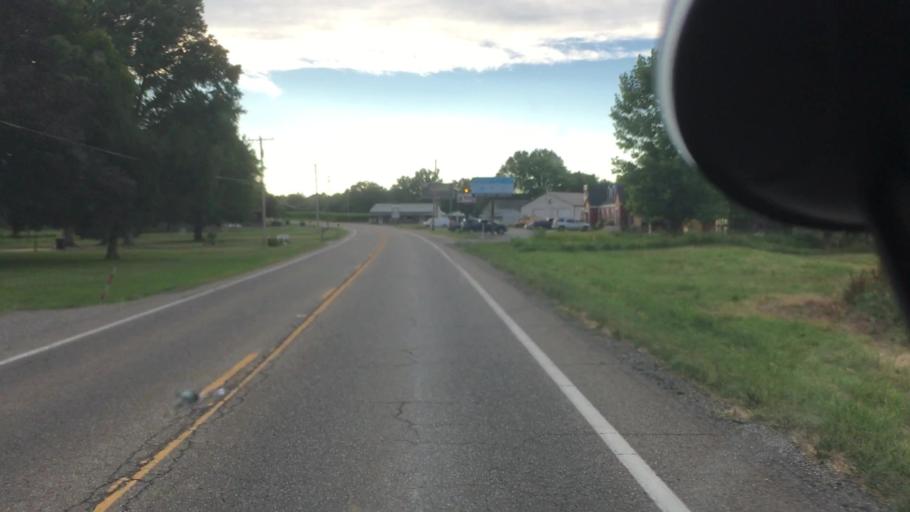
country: US
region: Ohio
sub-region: Columbiana County
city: New Waterford
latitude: 40.8735
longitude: -80.5861
